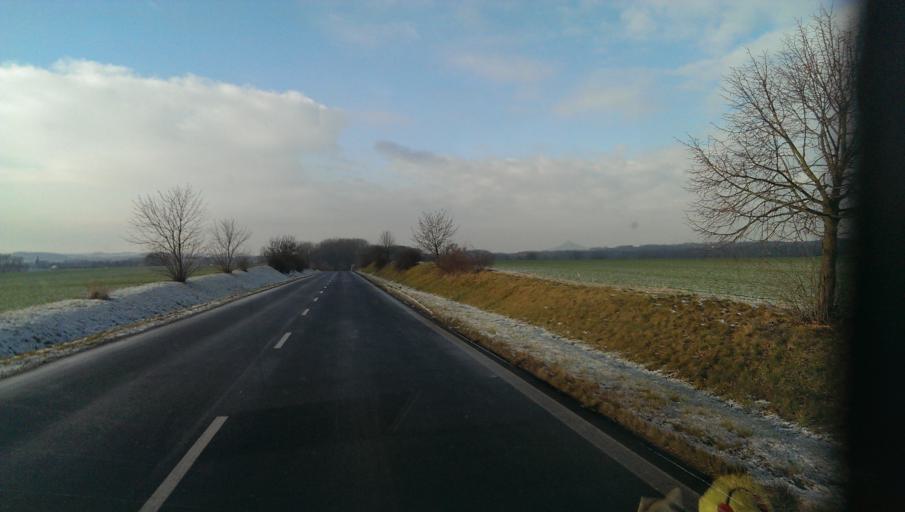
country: CZ
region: Ustecky
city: Budyne nad Ohri
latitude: 50.4067
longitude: 14.1541
